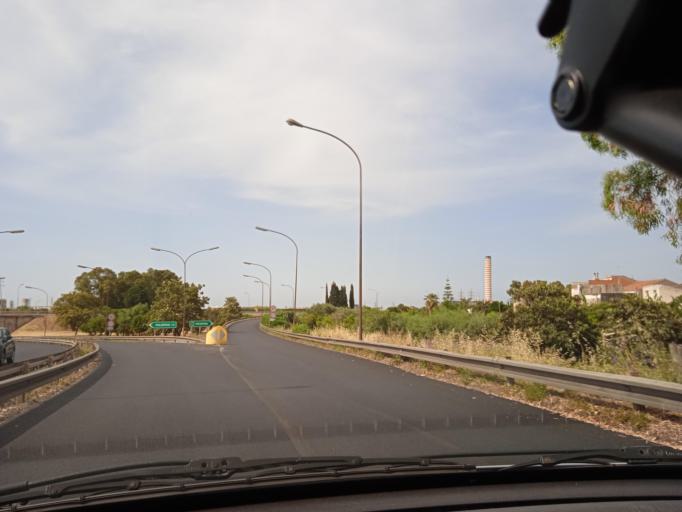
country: IT
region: Sicily
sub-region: Messina
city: San Filippo del Mela
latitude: 38.1903
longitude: 15.2747
